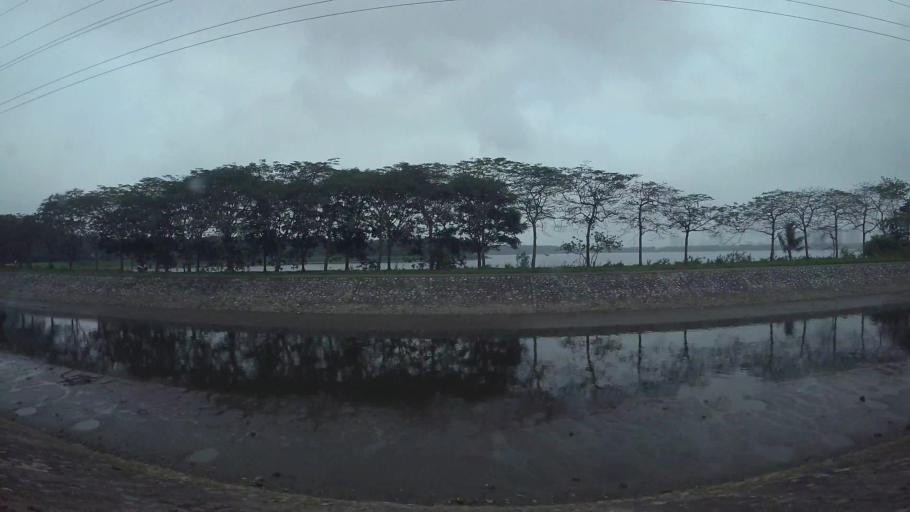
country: VN
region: Ha Noi
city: Van Dien
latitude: 20.9753
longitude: 105.8576
